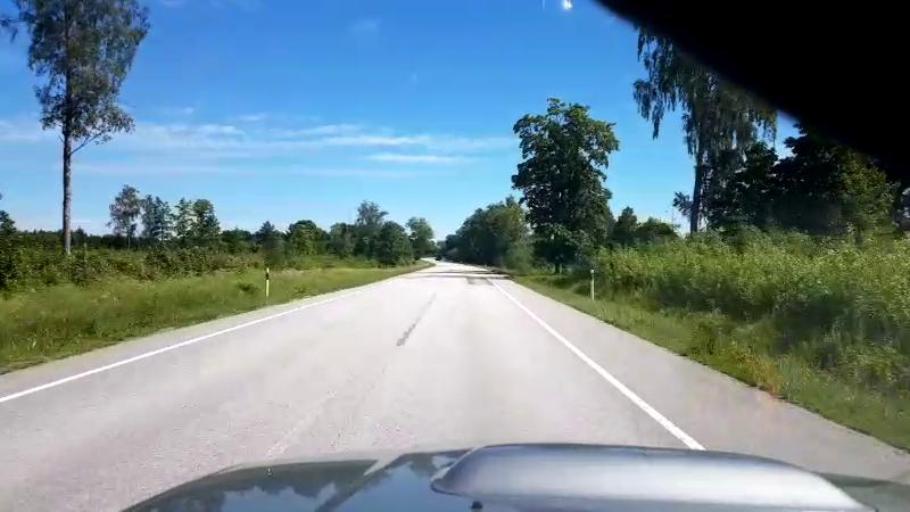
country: EE
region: Jaervamaa
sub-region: Koeru vald
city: Koeru
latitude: 58.9924
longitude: 25.9615
